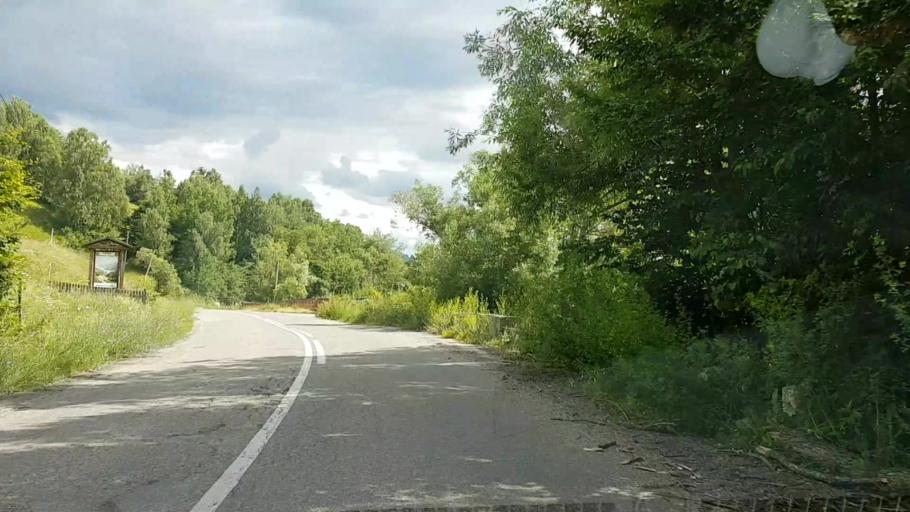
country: RO
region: Neamt
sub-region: Comuna Ceahlau
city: Ceahlau
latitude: 47.0667
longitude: 25.9608
